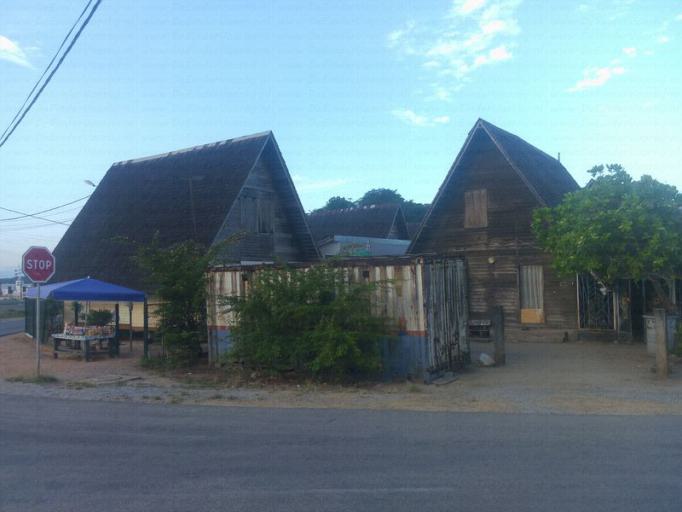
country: GF
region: Guyane
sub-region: Guyane
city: Saint-Laurent-du-Maroni
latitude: 5.4917
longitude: -54.0365
